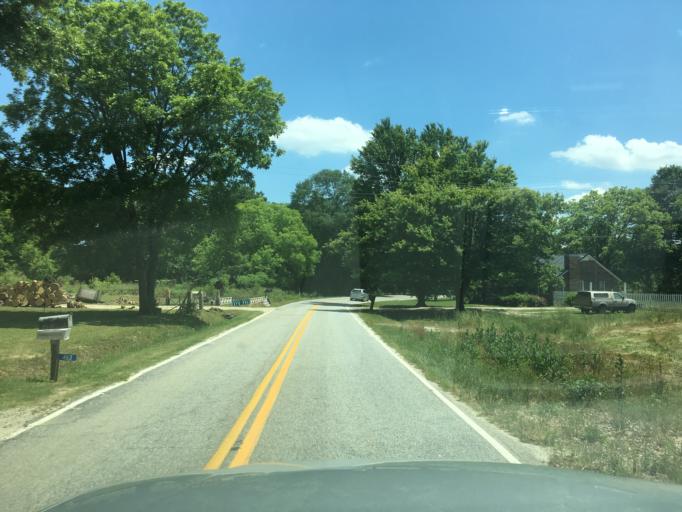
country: US
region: Georgia
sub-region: Hart County
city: Reed Creek
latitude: 34.5097
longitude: -82.9824
